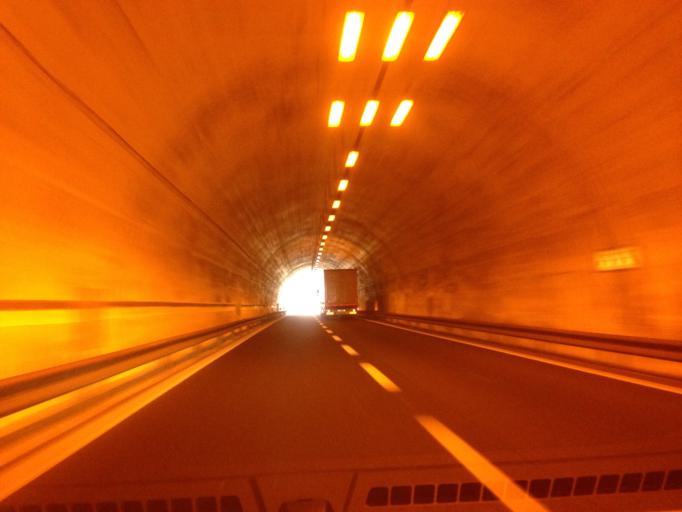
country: IT
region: Trentino-Alto Adige
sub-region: Bolzano
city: Ponte Gardena
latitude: 46.5733
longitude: 11.5233
